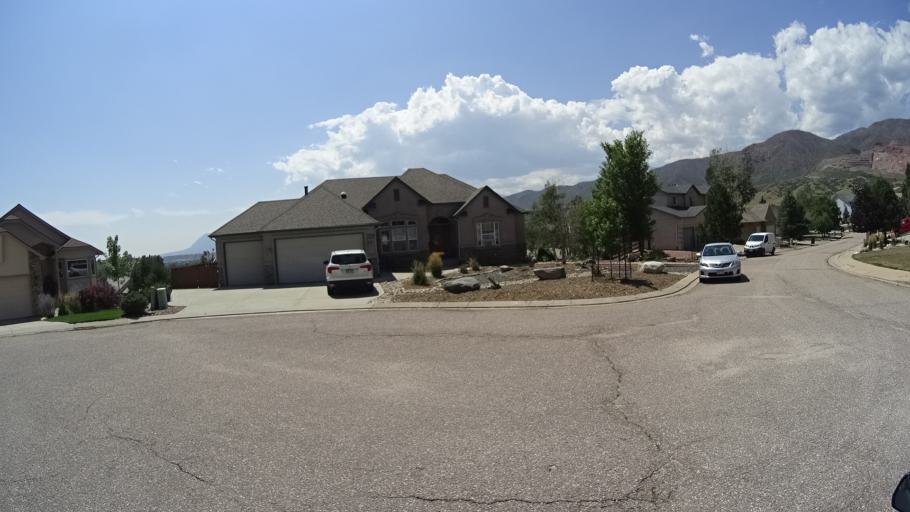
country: US
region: Colorado
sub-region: El Paso County
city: Air Force Academy
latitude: 38.9335
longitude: -104.8640
